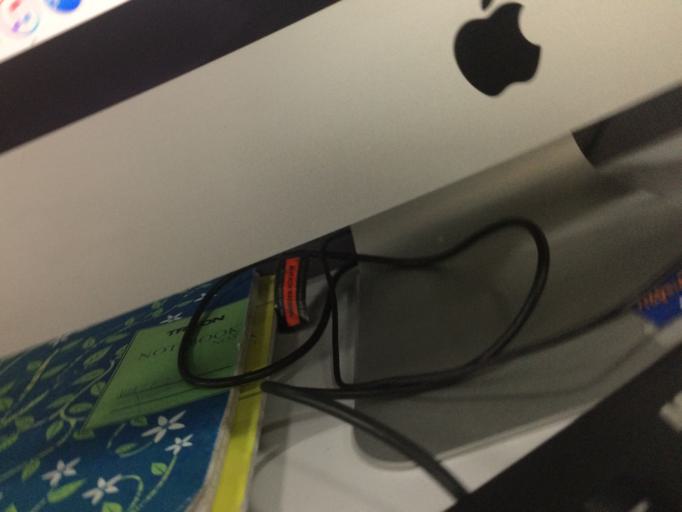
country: IN
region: Uttar Pradesh
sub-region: Gautam Buddha Nagar
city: Noida
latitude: 28.5496
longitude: 77.2680
